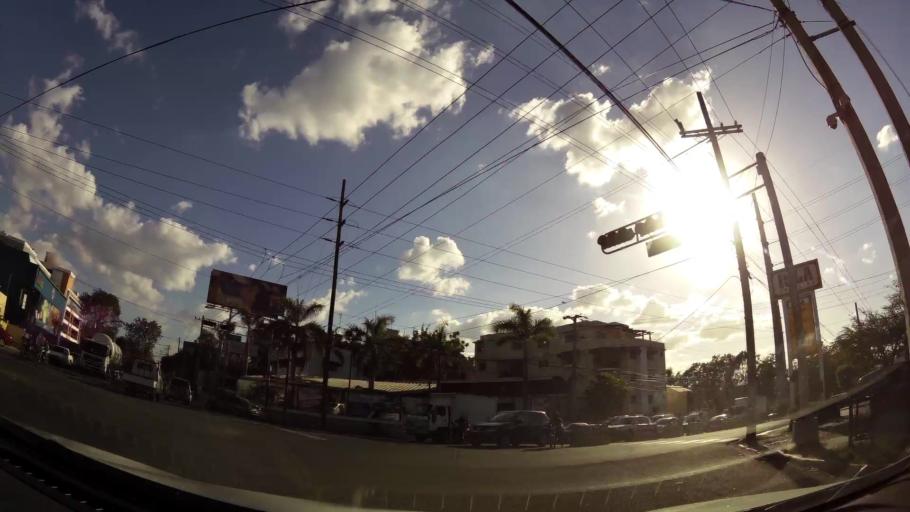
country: DO
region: Nacional
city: La Agustina
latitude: 18.5006
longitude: -69.9587
